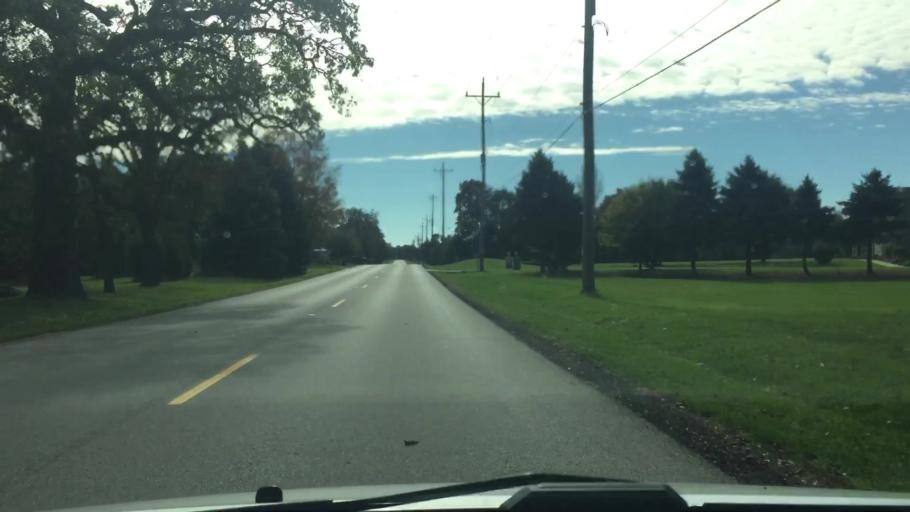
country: US
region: Wisconsin
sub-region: Waukesha County
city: Dousman
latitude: 43.0399
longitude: -88.4849
